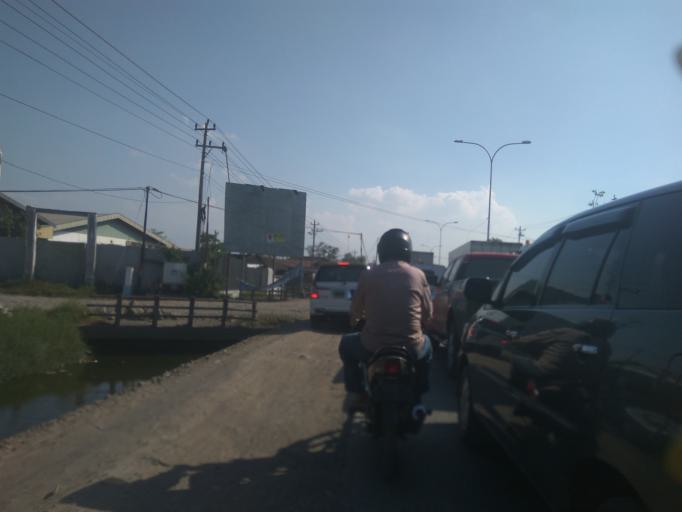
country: ID
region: Central Java
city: Semarang
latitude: -6.9544
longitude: 110.4733
